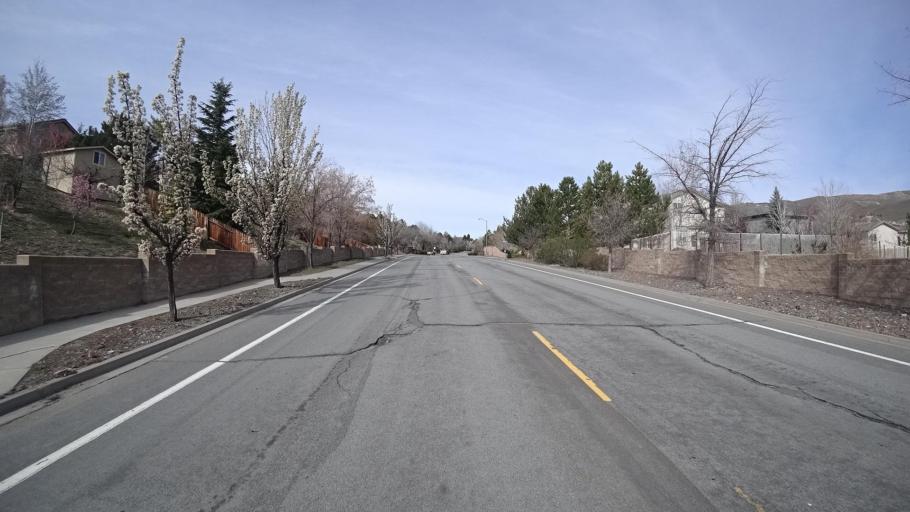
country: US
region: Nevada
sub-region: Washoe County
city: Mogul
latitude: 39.5434
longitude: -119.8809
